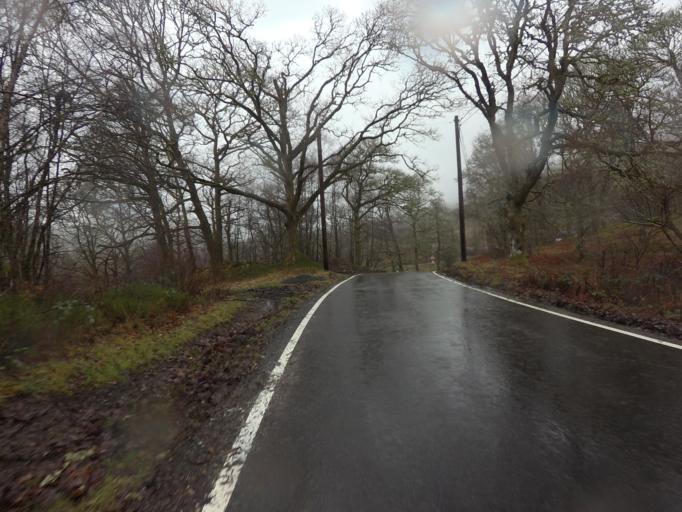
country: GB
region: Scotland
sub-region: West Dunbartonshire
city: Balloch
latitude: 56.1935
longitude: -4.5149
